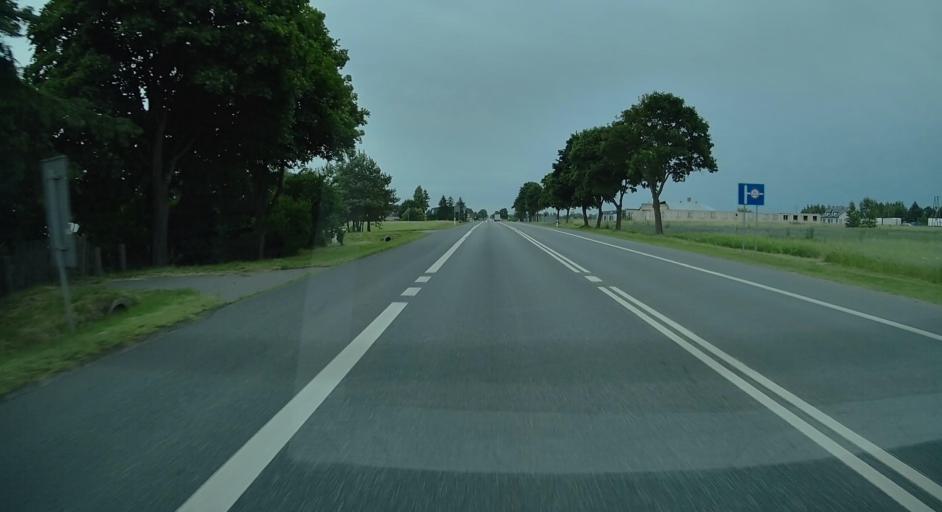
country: PL
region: Lublin Voivodeship
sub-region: Powiat bialski
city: Zalesie
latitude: 52.0349
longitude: 23.3244
